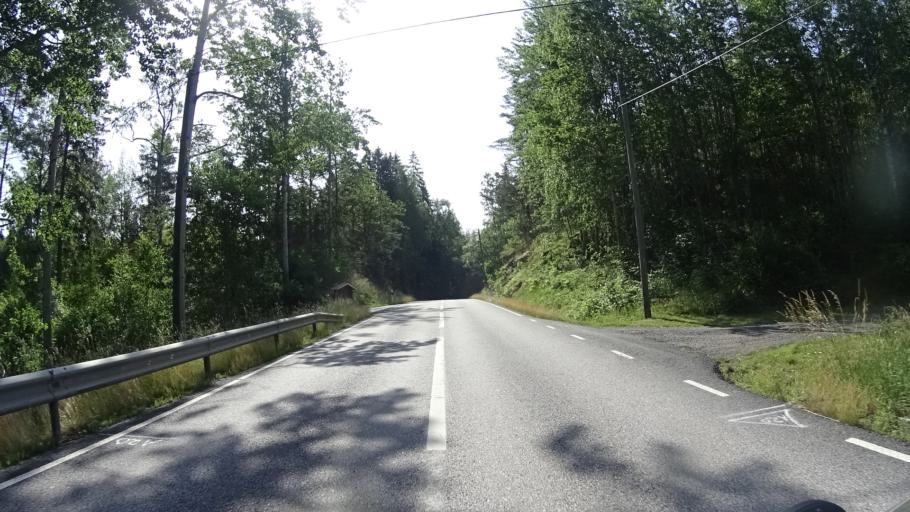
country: SE
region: Kalmar
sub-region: Vasterviks Kommun
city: Overum
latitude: 58.0320
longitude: 16.2343
